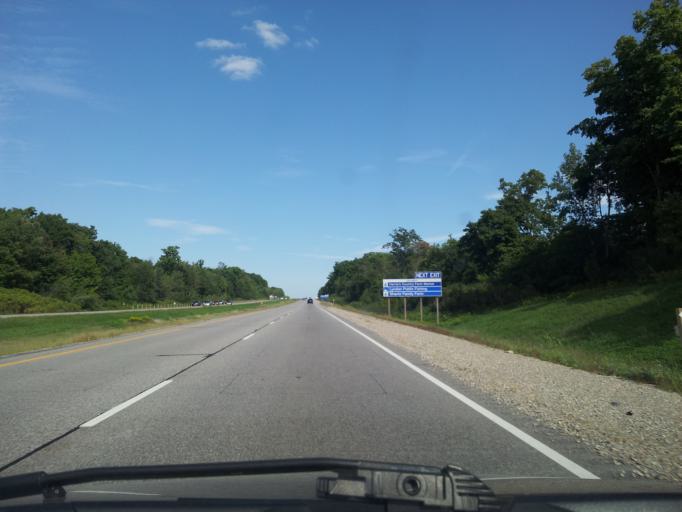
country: CA
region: Ontario
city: Kitchener
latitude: 43.3988
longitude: -80.6252
